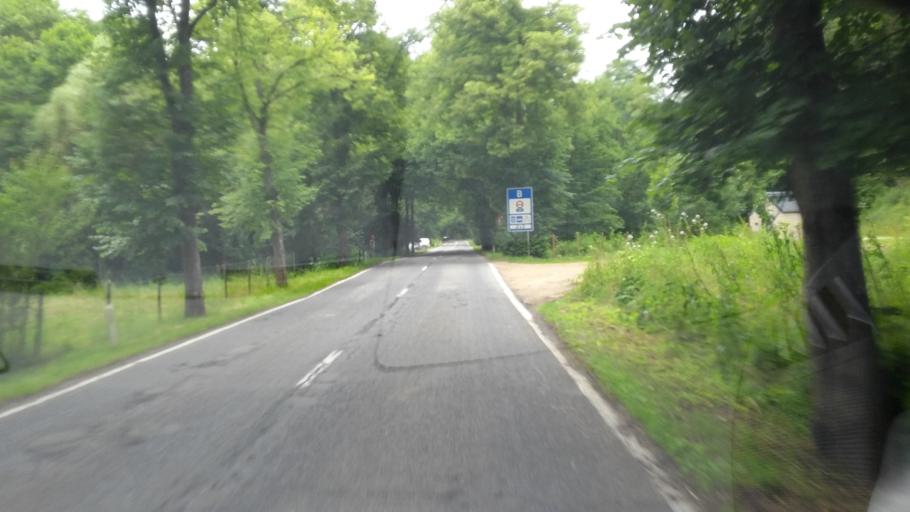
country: LU
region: Luxembourg
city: Eischen
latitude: 49.6950
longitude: 5.8645
